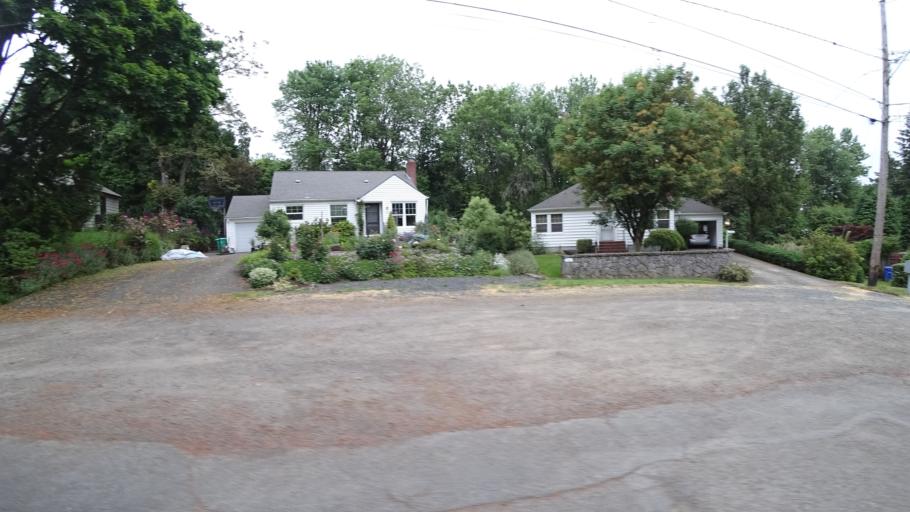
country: US
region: Oregon
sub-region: Multnomah County
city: Portland
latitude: 45.4873
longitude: -122.7088
